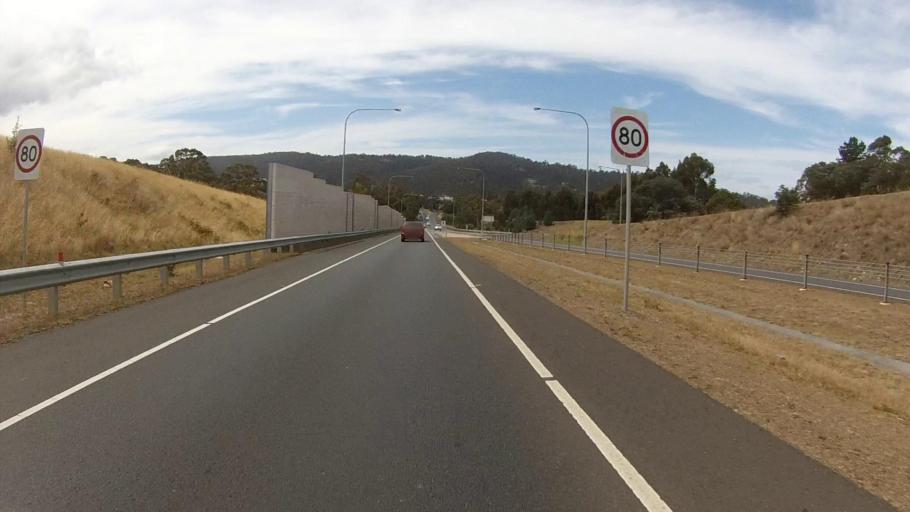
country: AU
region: Tasmania
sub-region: Kingborough
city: Kingston
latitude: -42.9743
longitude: 147.3037
